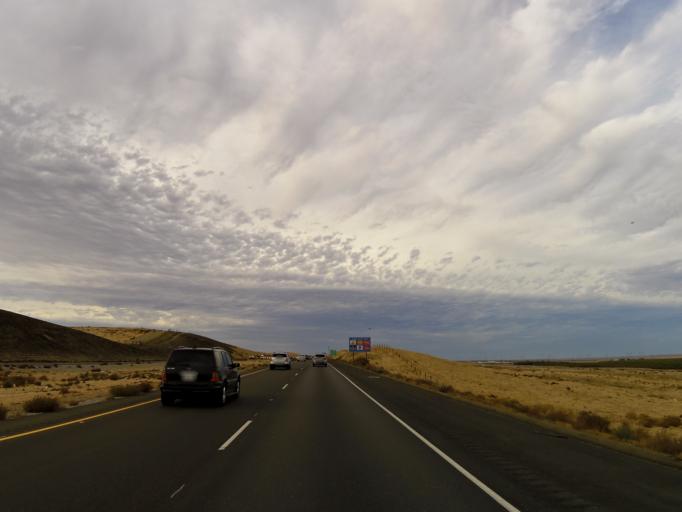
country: US
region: California
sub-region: Kings County
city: Kettleman City
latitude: 35.9678
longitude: -119.9458
